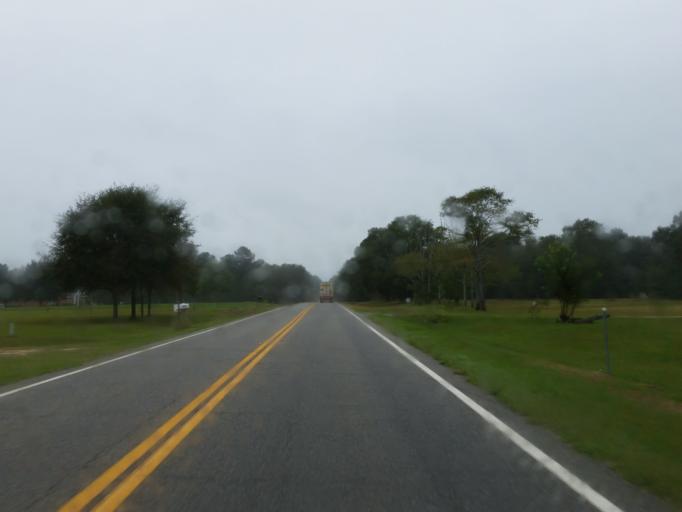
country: US
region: Georgia
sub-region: Berrien County
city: Ray City
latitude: 31.1020
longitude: -83.2754
